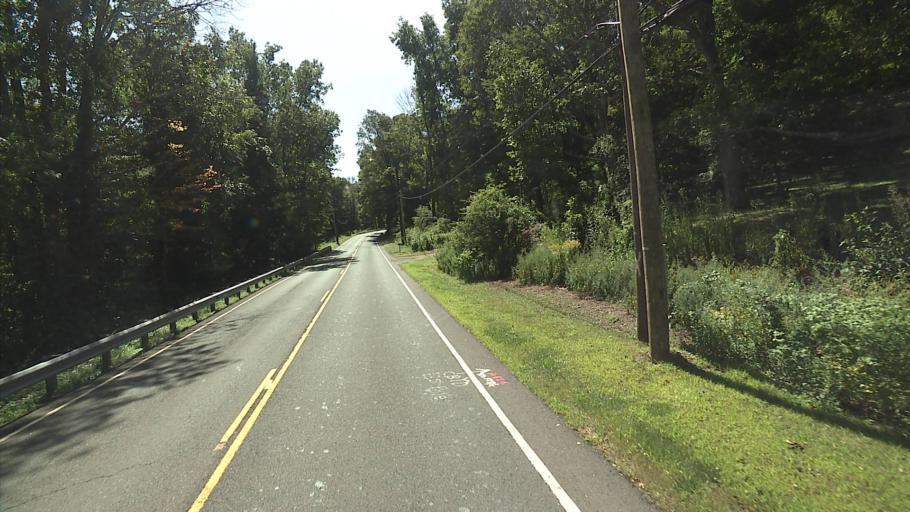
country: US
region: Connecticut
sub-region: New Haven County
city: Southbury
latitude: 41.4754
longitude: -73.1590
